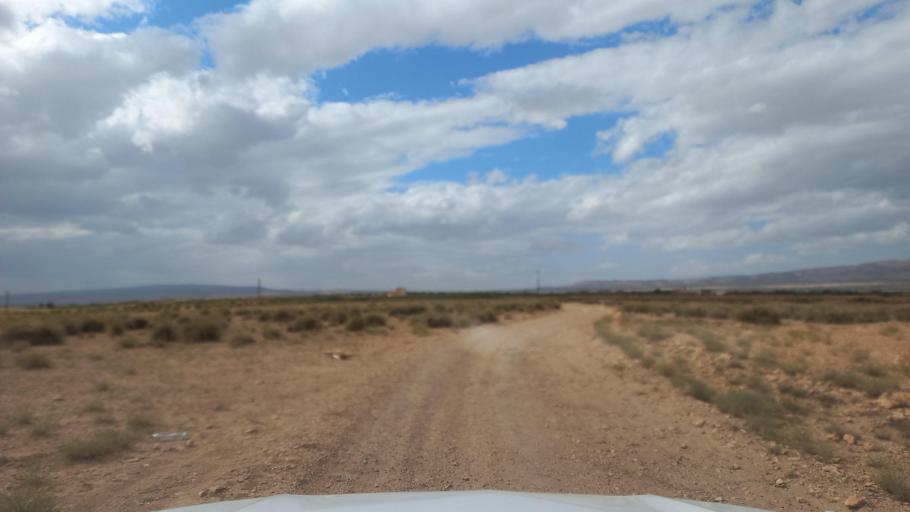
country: TN
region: Al Qasrayn
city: Sbiba
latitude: 35.3810
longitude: 9.1012
